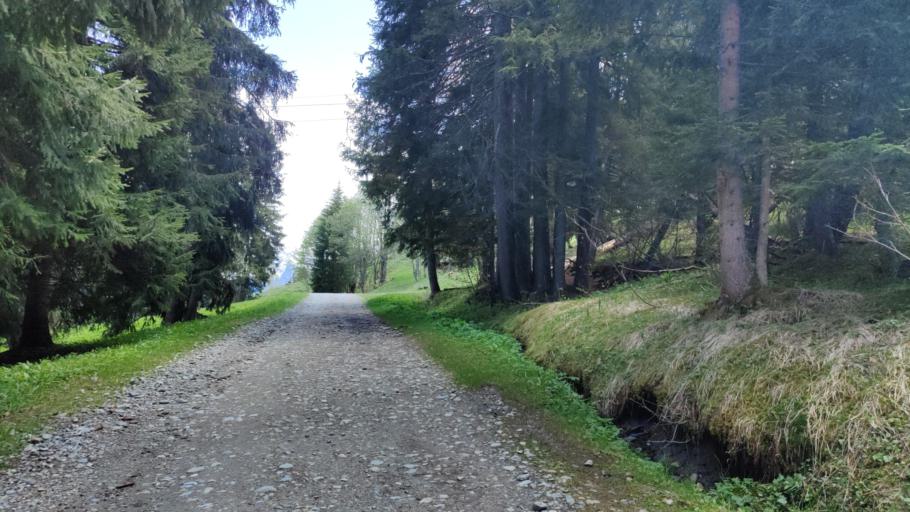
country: FR
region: Rhone-Alpes
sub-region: Departement de la Haute-Savoie
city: Saint-Gervais-les-Bains
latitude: 45.8756
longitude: 6.6823
